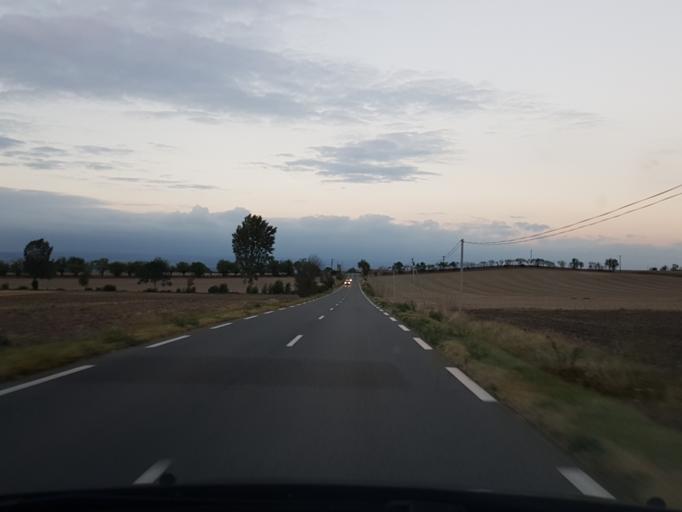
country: FR
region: Languedoc-Roussillon
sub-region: Departement de l'Aude
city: Bram
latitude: 43.2163
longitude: 2.0768
